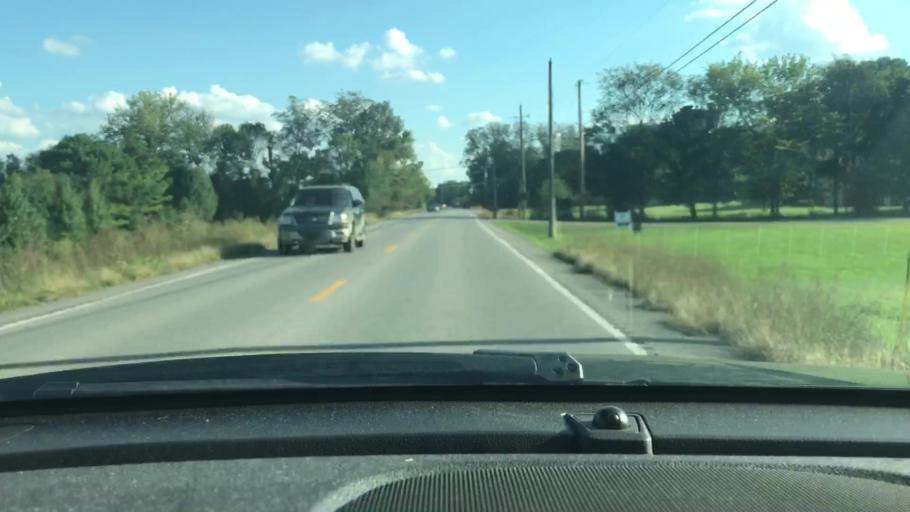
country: US
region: Tennessee
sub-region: Sumner County
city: Shackle Island
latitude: 36.3843
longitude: -86.6213
